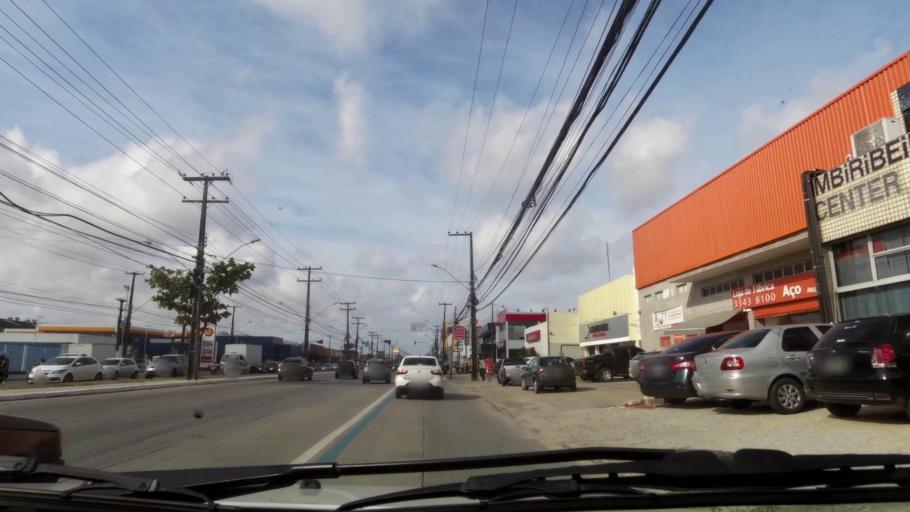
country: BR
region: Pernambuco
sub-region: Recife
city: Recife
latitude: -8.1072
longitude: -34.9116
